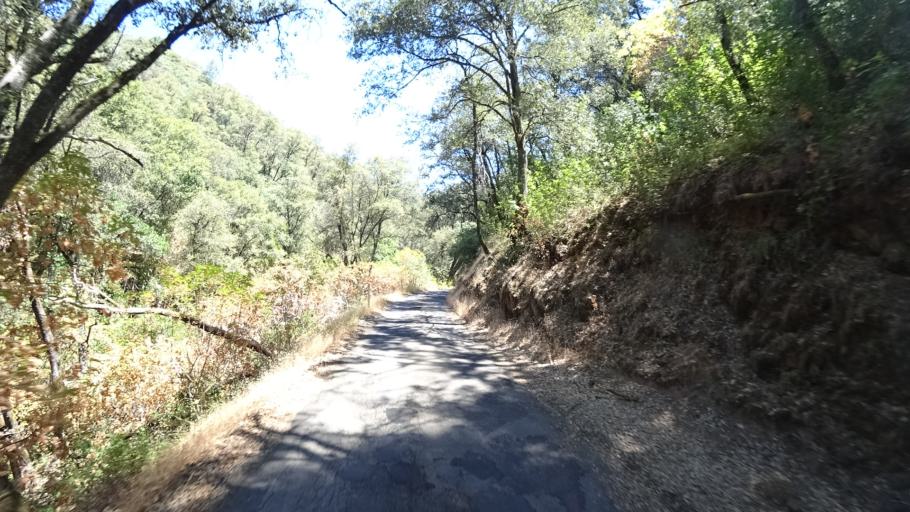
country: US
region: California
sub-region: Calaveras County
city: Murphys
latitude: 38.1383
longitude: -120.4255
